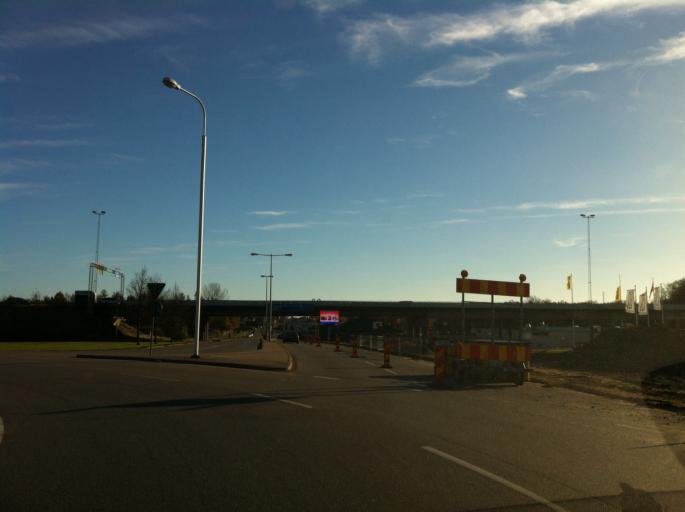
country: SE
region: Blekinge
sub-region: Karlshamns Kommun
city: Karlshamn
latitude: 56.1893
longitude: 14.8533
